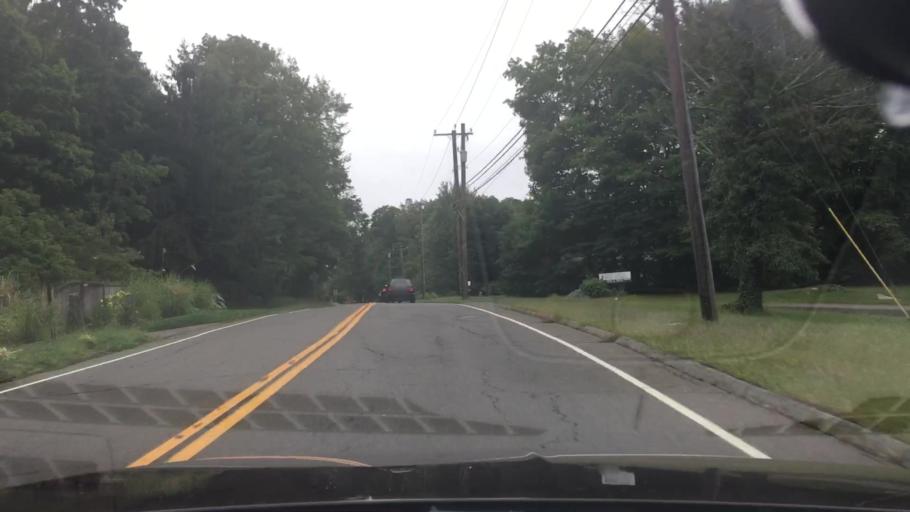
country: US
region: Connecticut
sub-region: Middlesex County
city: Higganum
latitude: 41.4477
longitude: -72.5551
